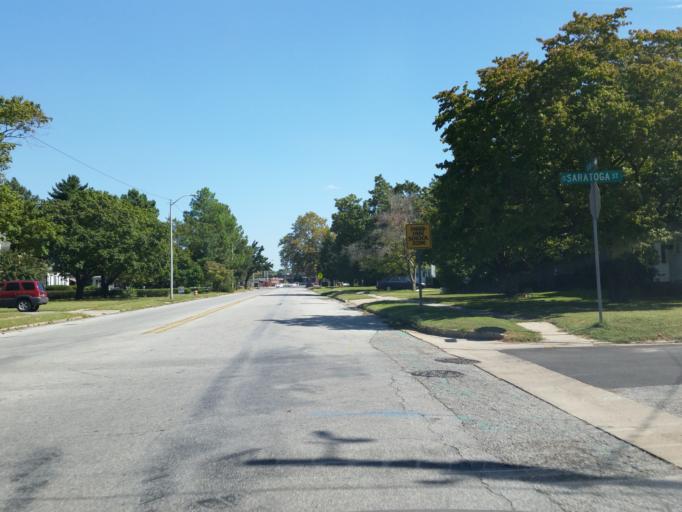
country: US
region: Maryland
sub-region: Wicomico County
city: Salisbury
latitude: 38.3714
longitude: -75.5784
